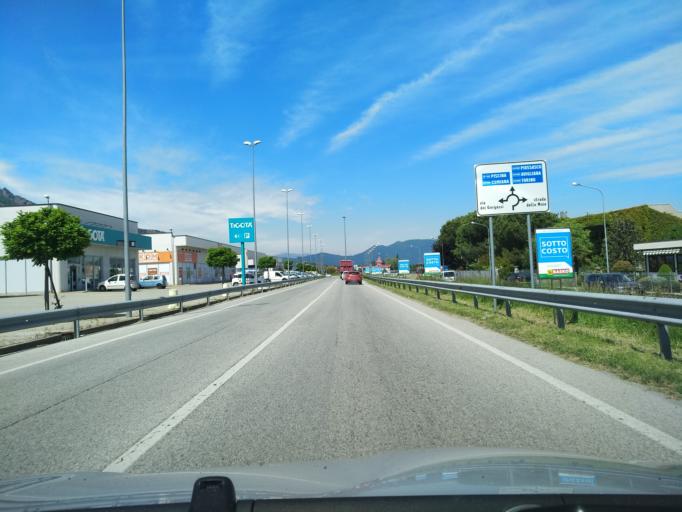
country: IT
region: Piedmont
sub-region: Provincia di Torino
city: Frossasco
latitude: 44.9263
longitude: 7.3681
